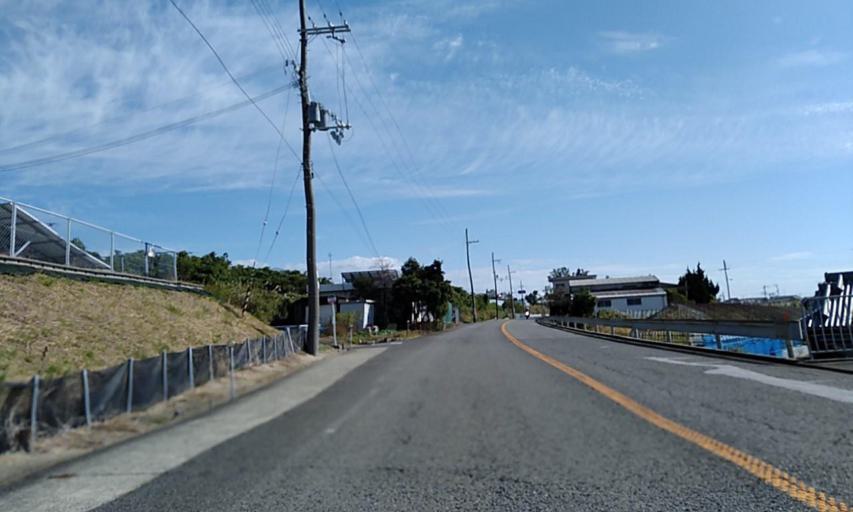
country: JP
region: Wakayama
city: Gobo
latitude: 33.8256
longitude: 135.1890
